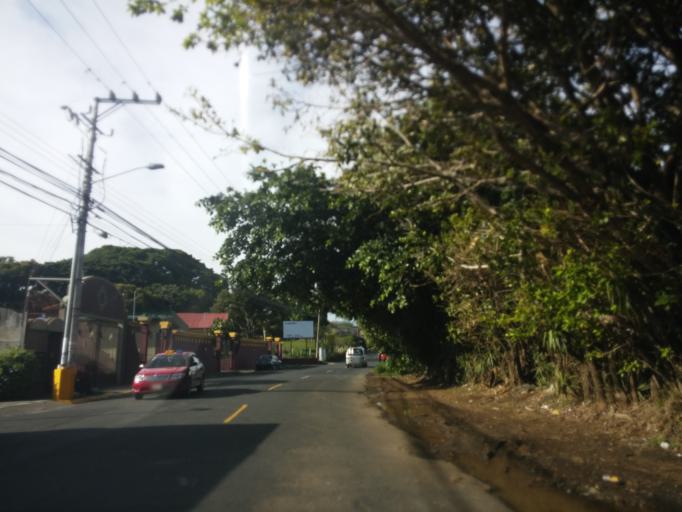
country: CR
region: Heredia
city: Llorente
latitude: 10.0083
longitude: -84.1521
